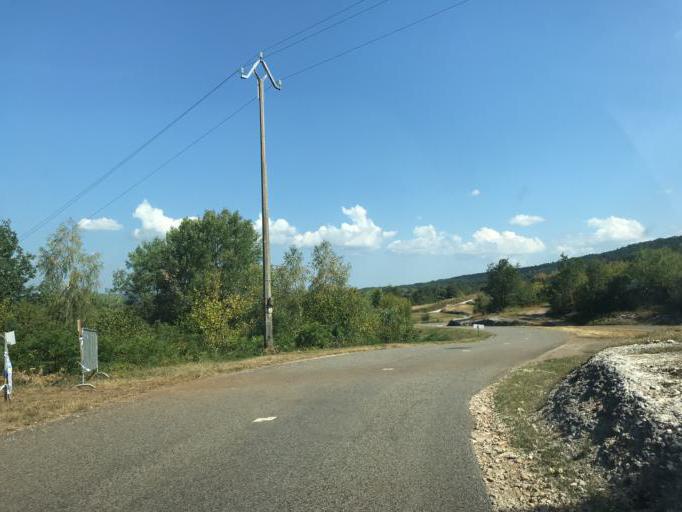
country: FR
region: Franche-Comte
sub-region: Departement du Jura
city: Moirans-en-Montagne
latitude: 46.4620
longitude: 5.7255
